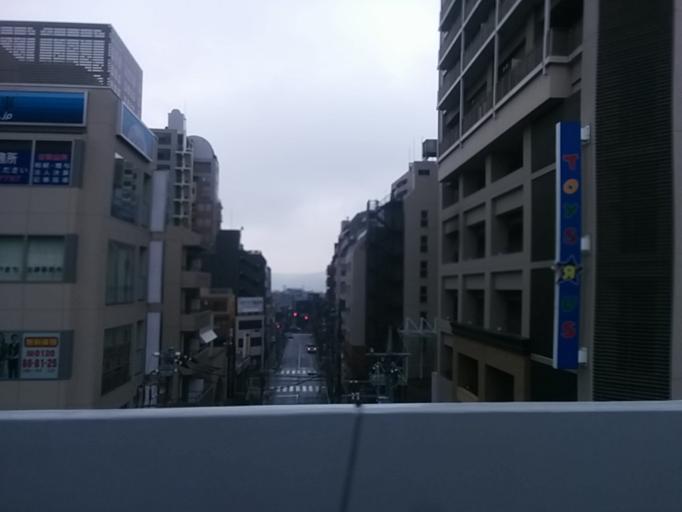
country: JP
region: Tokyo
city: Kokubunji
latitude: 35.6718
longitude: 139.4819
